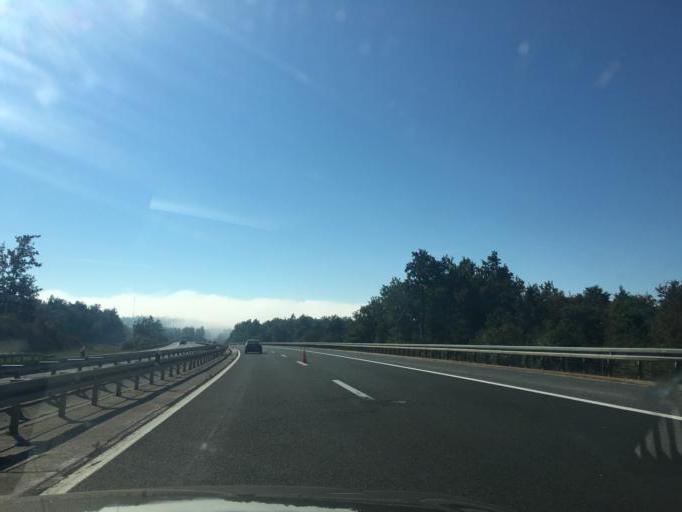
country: HR
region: Licko-Senjska
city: Gospic
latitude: 44.6435
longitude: 15.4351
